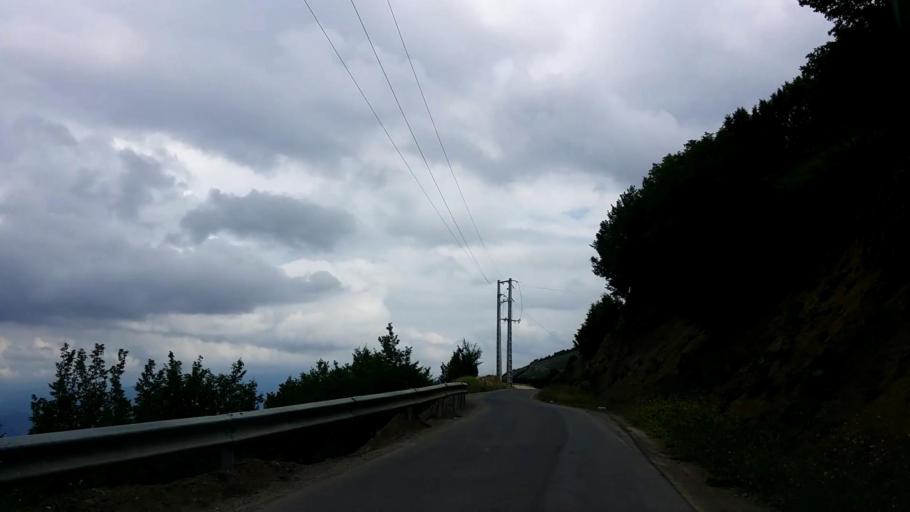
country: IR
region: Mazandaran
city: Chalus
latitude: 36.5519
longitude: 51.2701
